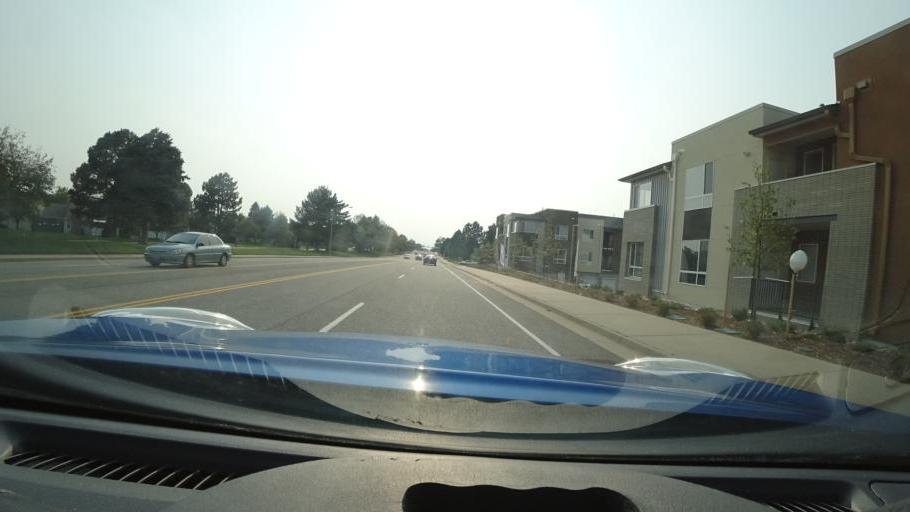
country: US
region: Colorado
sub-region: Adams County
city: Aurora
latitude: 39.6677
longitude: -104.8248
